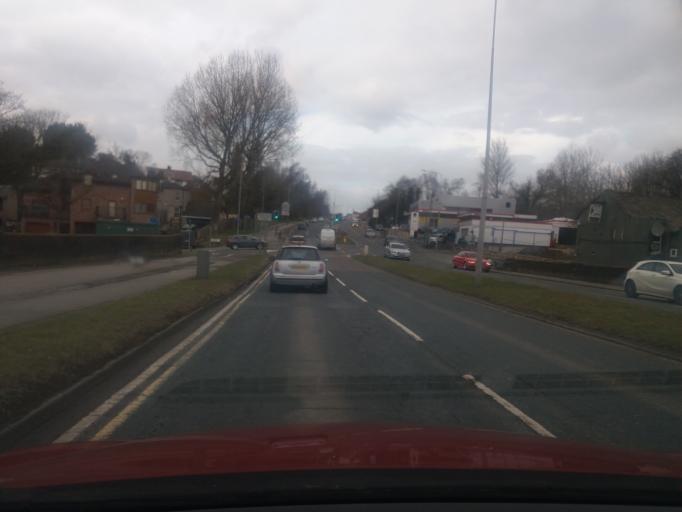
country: GB
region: England
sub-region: Lancashire
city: Preston
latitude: 53.7530
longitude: -2.6798
